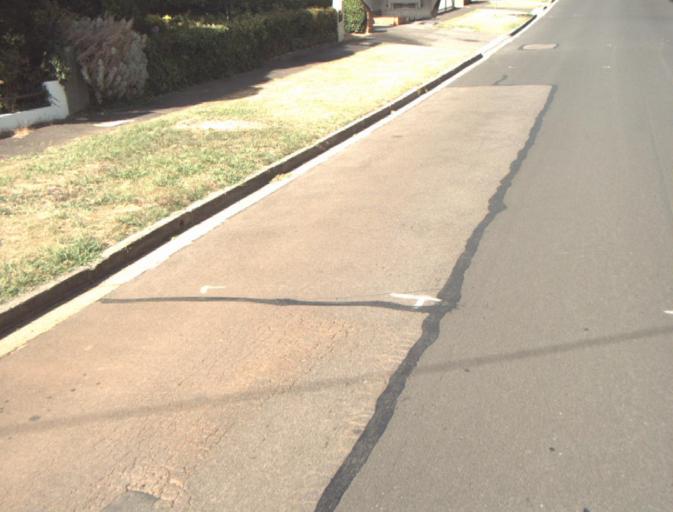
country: AU
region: Tasmania
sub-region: Launceston
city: East Launceston
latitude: -41.4499
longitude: 147.1620
